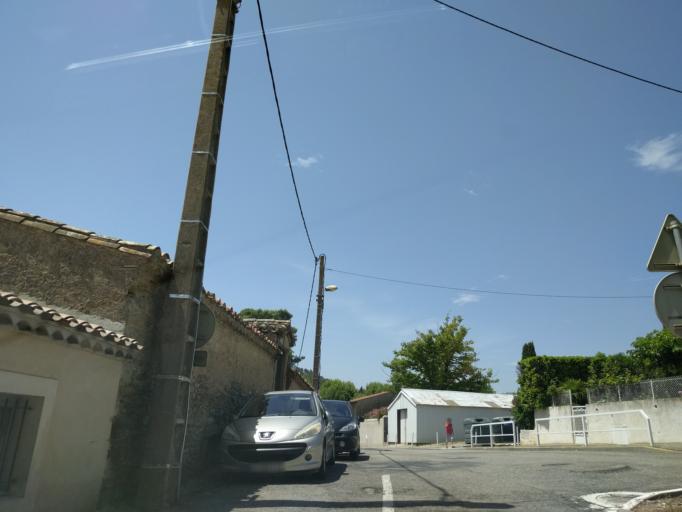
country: FR
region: Languedoc-Roussillon
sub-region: Departement de l'Aude
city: Palaja
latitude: 43.2019
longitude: 2.3951
